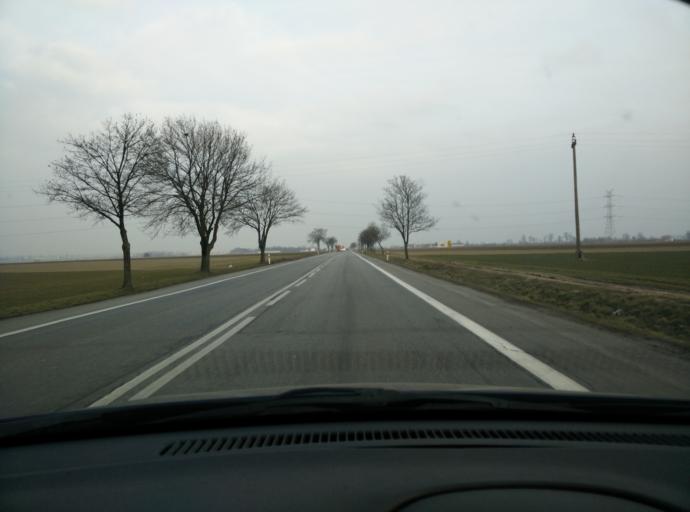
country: PL
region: Greater Poland Voivodeship
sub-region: Powiat sredzki
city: Sroda Wielkopolska
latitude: 52.2299
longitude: 17.2029
